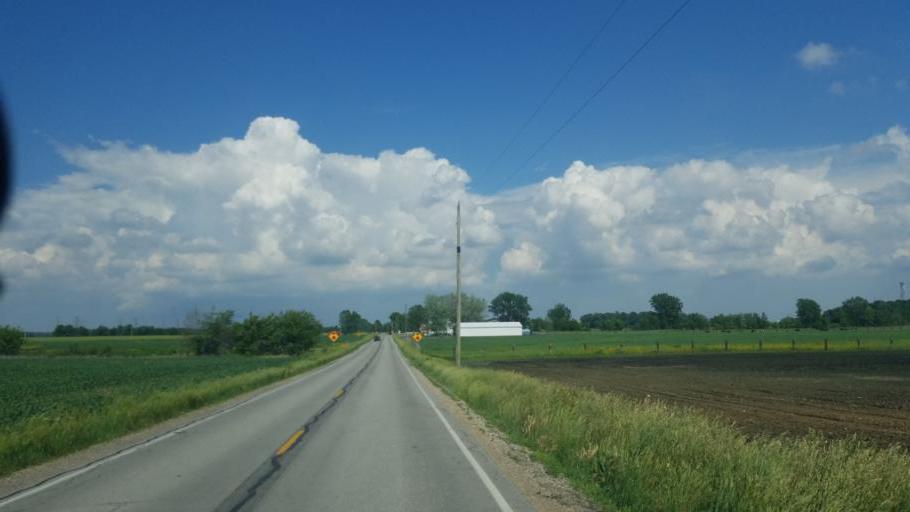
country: US
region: Indiana
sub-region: Marshall County
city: Bourbon
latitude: 41.3144
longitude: -86.0442
